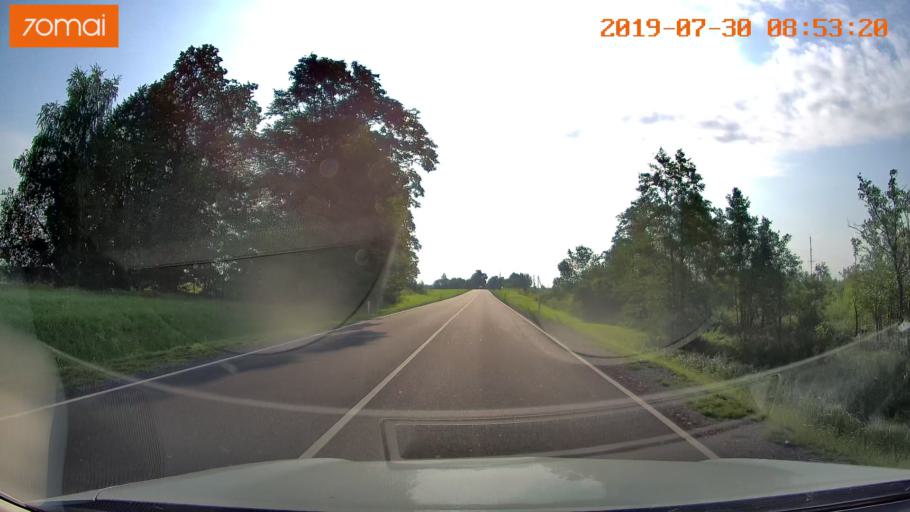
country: RU
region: Kaliningrad
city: Chernyakhovsk
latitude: 54.6018
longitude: 21.9955
